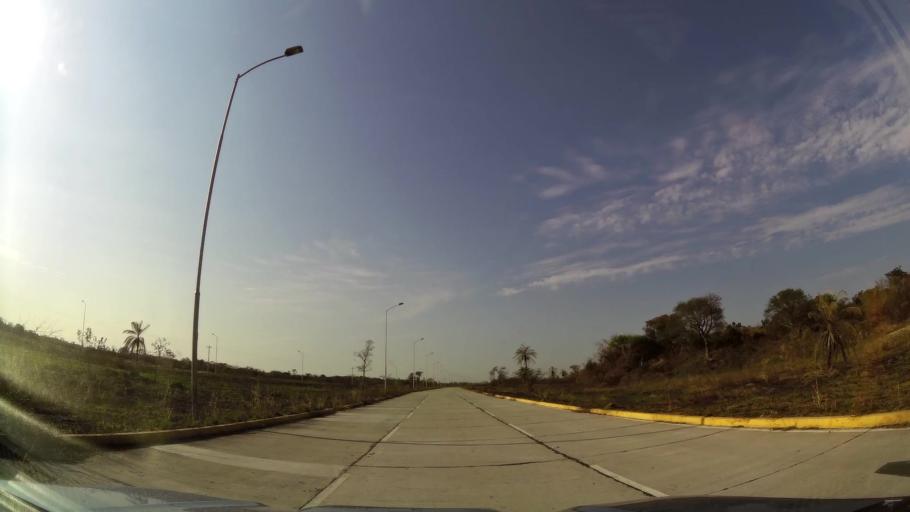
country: BO
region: Santa Cruz
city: Santa Cruz de la Sierra
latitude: -17.6677
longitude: -63.1305
